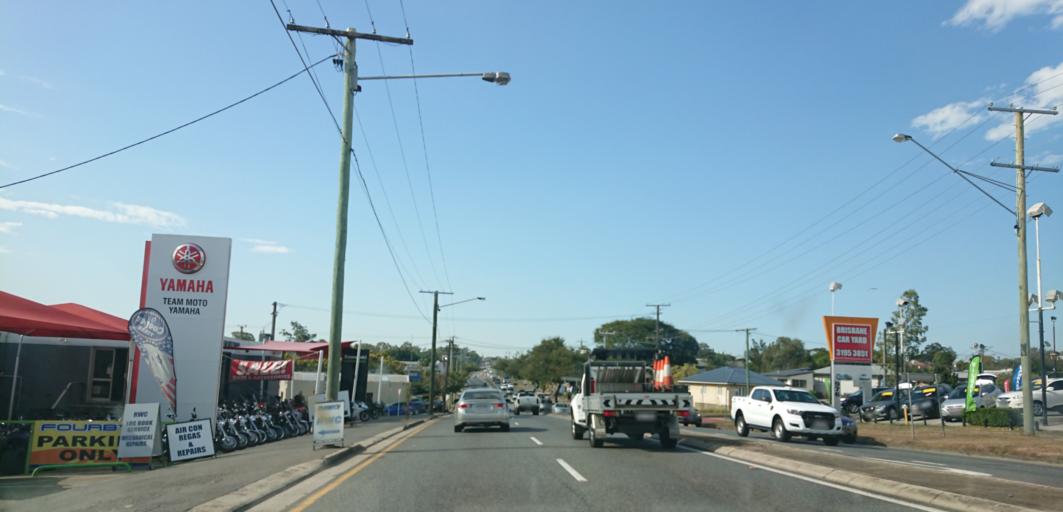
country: AU
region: Queensland
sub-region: Brisbane
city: Yeerongpilly
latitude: -27.5295
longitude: 153.0189
